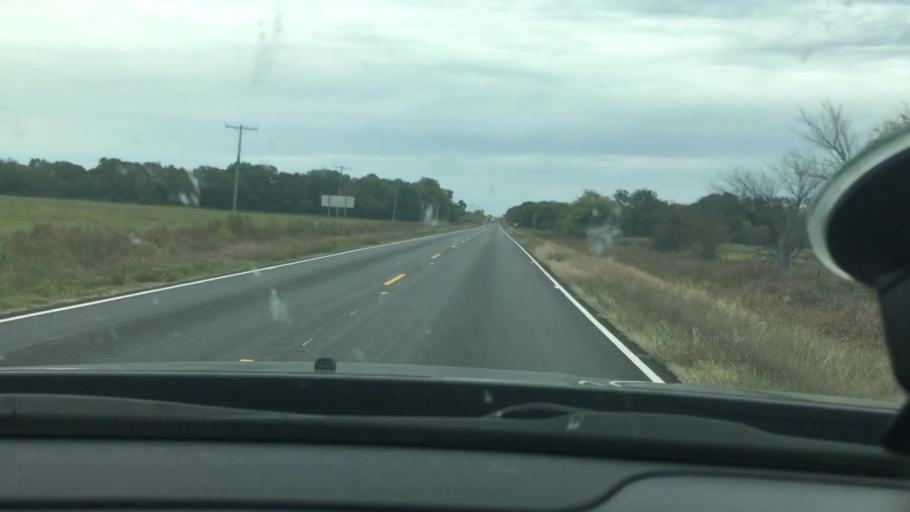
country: US
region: Oklahoma
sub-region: Coal County
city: Coalgate
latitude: 34.4016
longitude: -96.4245
